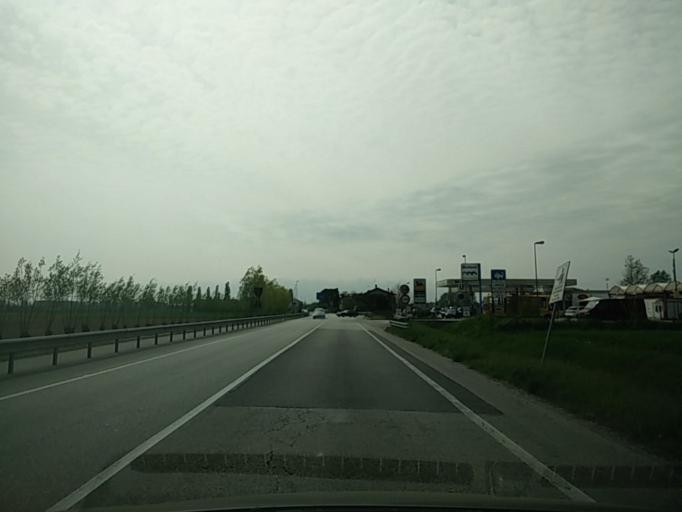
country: IT
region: Veneto
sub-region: Provincia di Venezia
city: Marano
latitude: 45.4667
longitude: 12.1080
